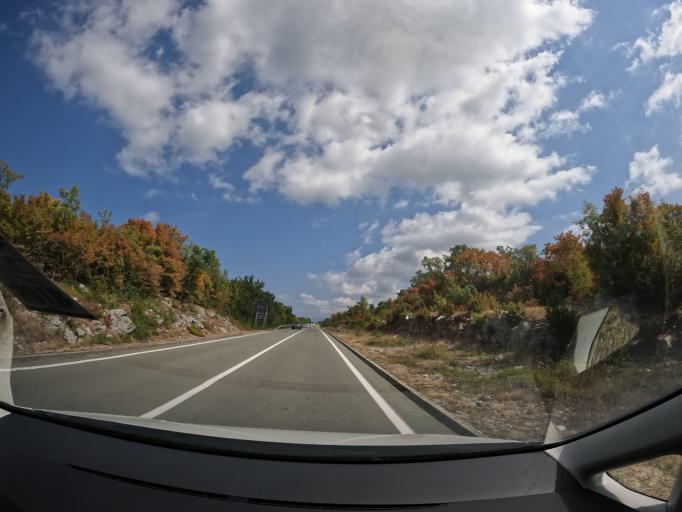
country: HR
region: Primorsko-Goranska
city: Njivice
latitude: 45.1053
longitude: 14.5427
